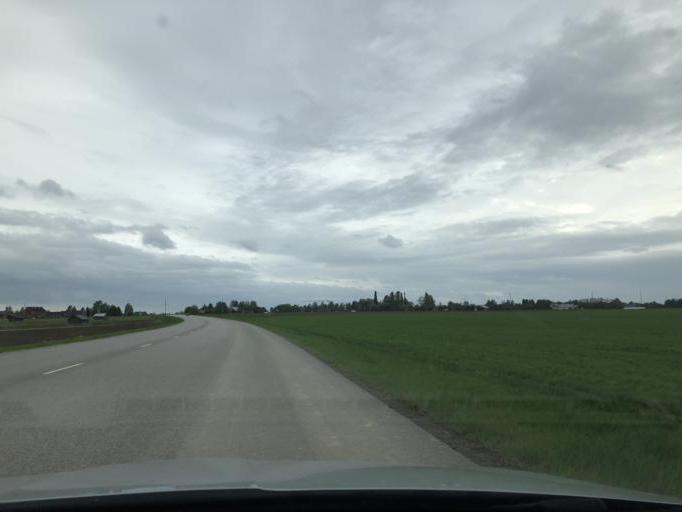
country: SE
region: Norrbotten
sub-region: Pitea Kommun
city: Bergsviken
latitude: 65.3616
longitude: 21.4045
